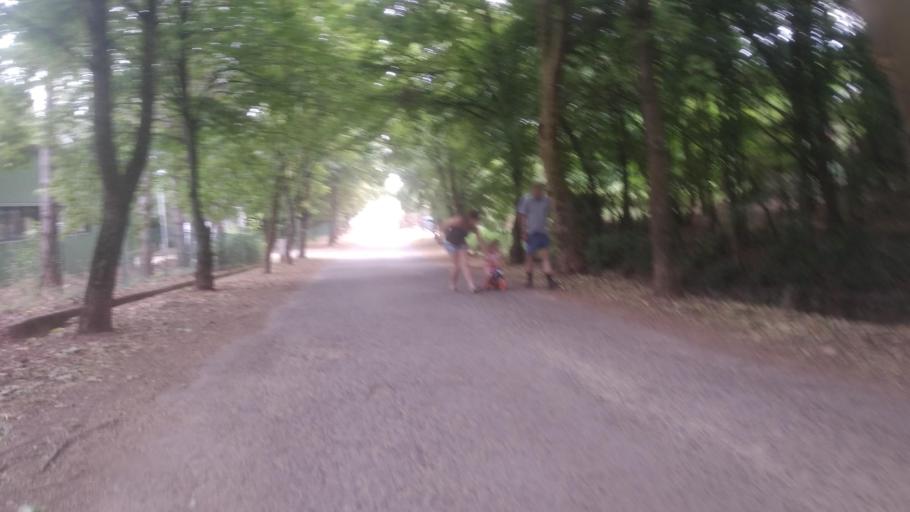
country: HU
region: Veszprem
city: Csopak
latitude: 46.9980
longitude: 17.9739
